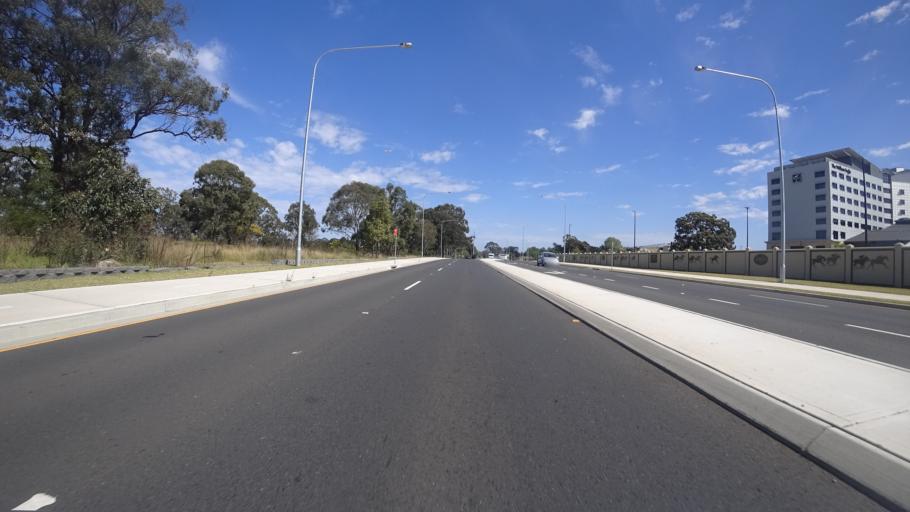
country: AU
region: New South Wales
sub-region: Fairfield
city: Chipping Norton
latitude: -33.9156
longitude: 150.9465
